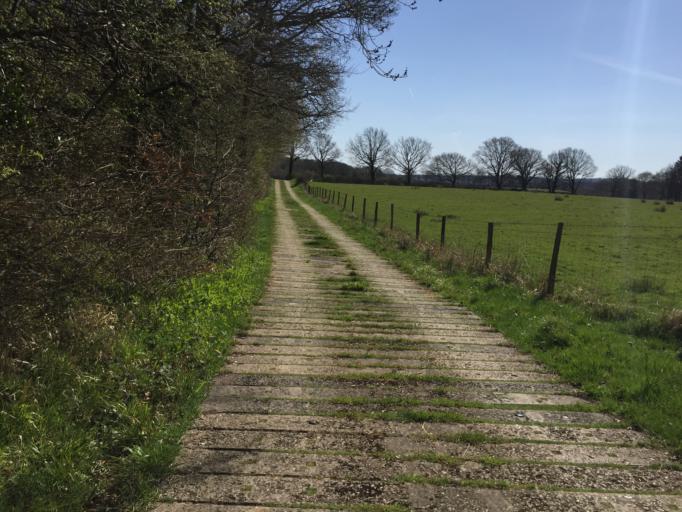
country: GB
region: England
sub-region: East Sussex
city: Wadhurst
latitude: 51.0286
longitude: 0.2890
